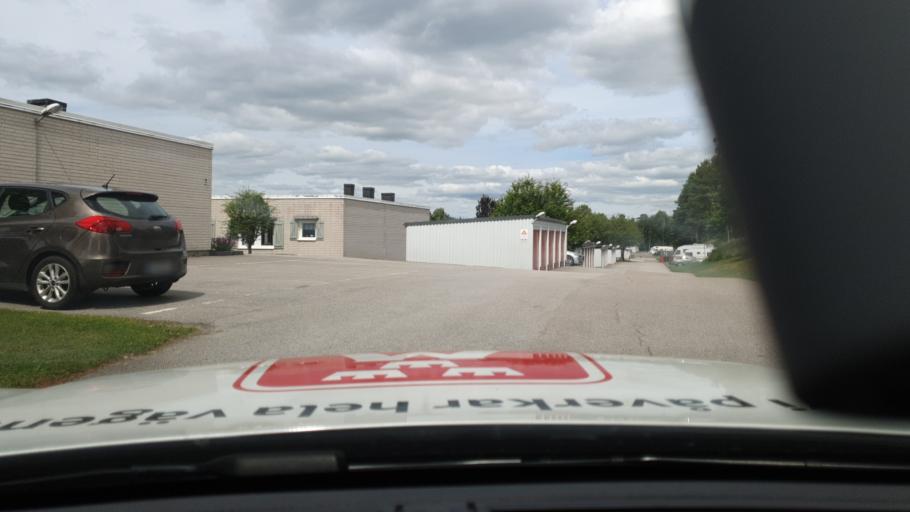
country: SE
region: Vaestra Goetaland
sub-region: Skovde Kommun
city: Stopen
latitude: 58.4231
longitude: 13.8839
